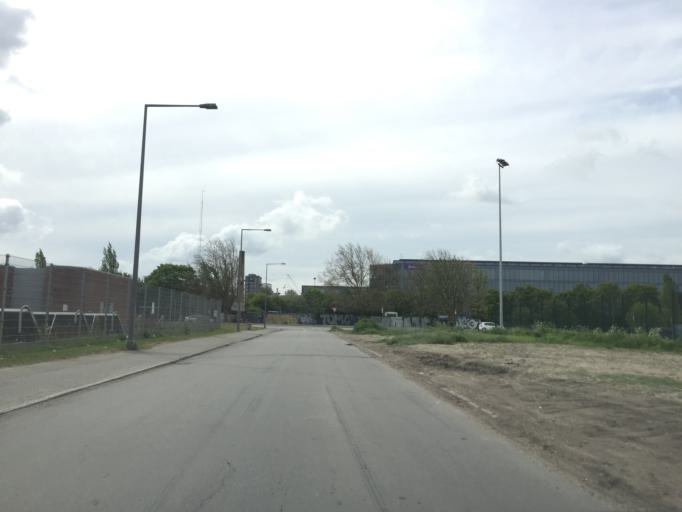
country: DK
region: Capital Region
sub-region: Kobenhavn
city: Christianshavn
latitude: 55.6702
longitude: 12.6206
